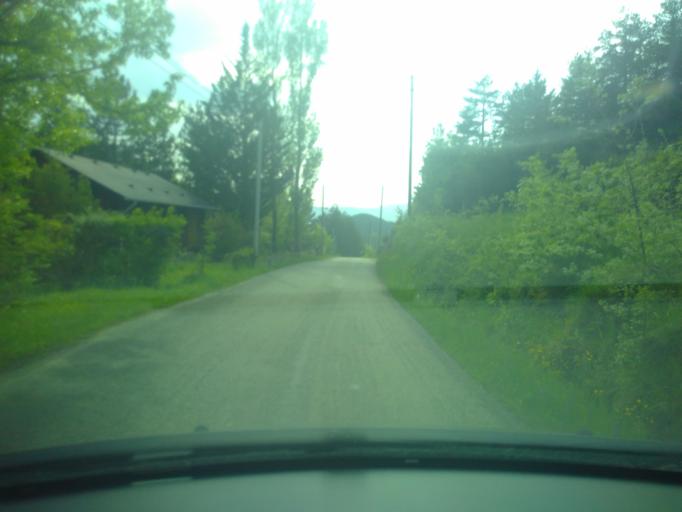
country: FR
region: Rhone-Alpes
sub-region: Departement de la Drome
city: Die
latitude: 44.6724
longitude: 5.4835
